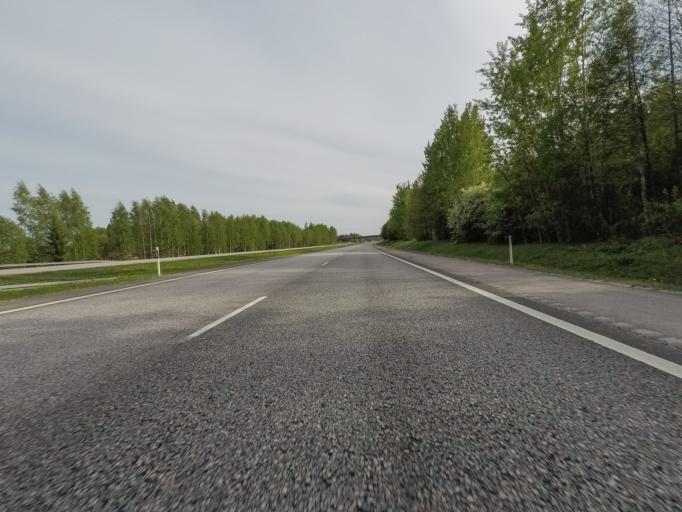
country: FI
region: Uusimaa
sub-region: Helsinki
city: Nurmijaervi
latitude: 60.4660
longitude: 24.8494
